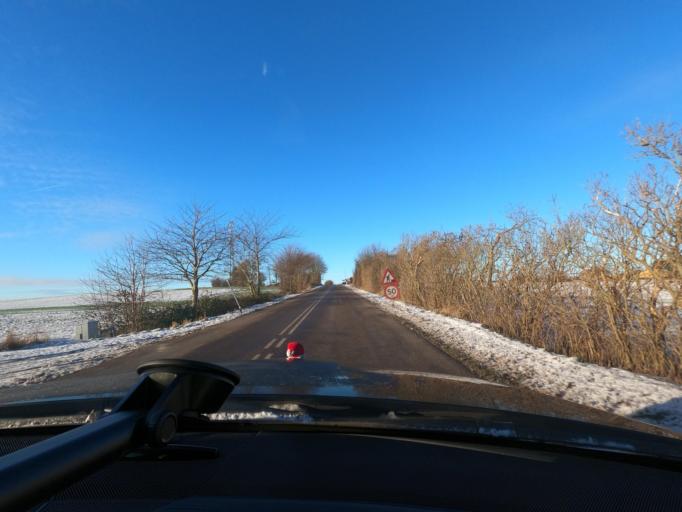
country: DK
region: South Denmark
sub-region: Sonderborg Kommune
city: Horuphav
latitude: 54.8742
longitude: 9.9292
